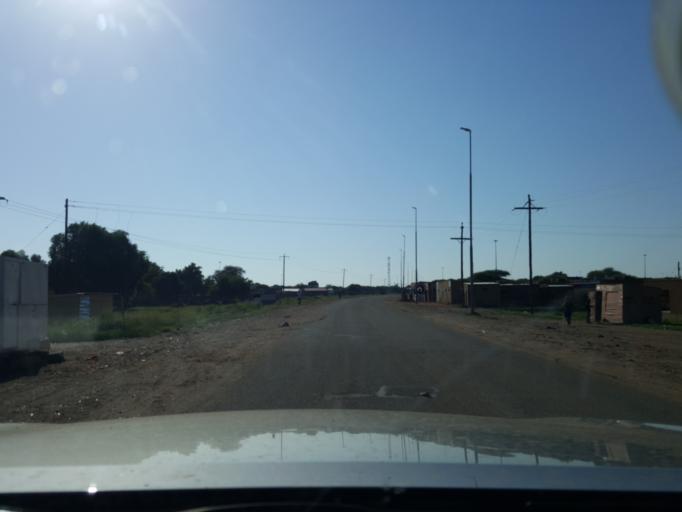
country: ZA
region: North-West
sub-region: Ngaka Modiri Molema District Municipality
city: Mmabatho
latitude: -25.8265
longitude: 25.6454
